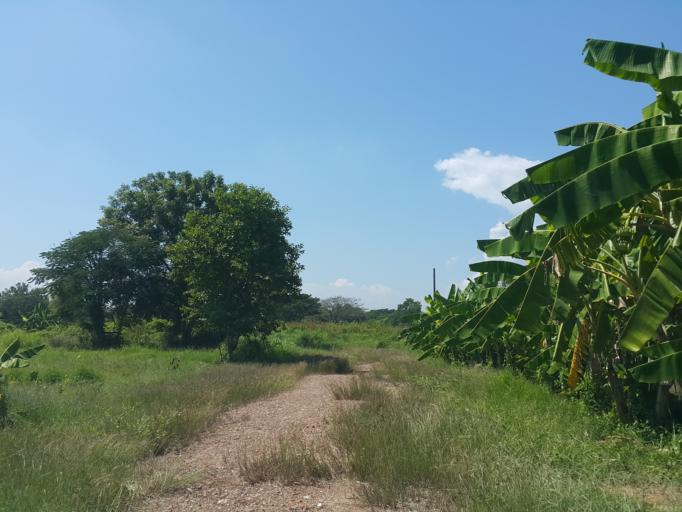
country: TH
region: Chiang Mai
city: Saraphi
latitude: 18.7675
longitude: 99.0594
